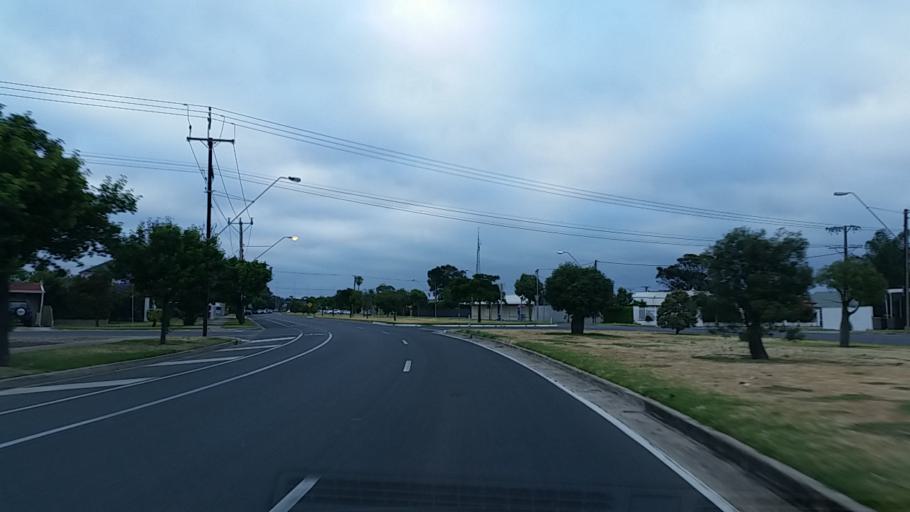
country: AU
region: South Australia
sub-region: City of West Torrens
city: Plympton
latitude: -34.9284
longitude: 138.5431
